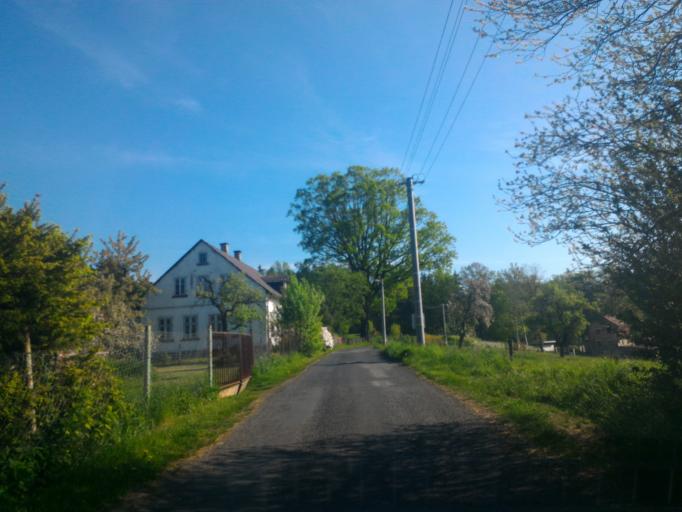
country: CZ
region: Ustecky
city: Varnsdorf
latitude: 50.9173
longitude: 14.6430
